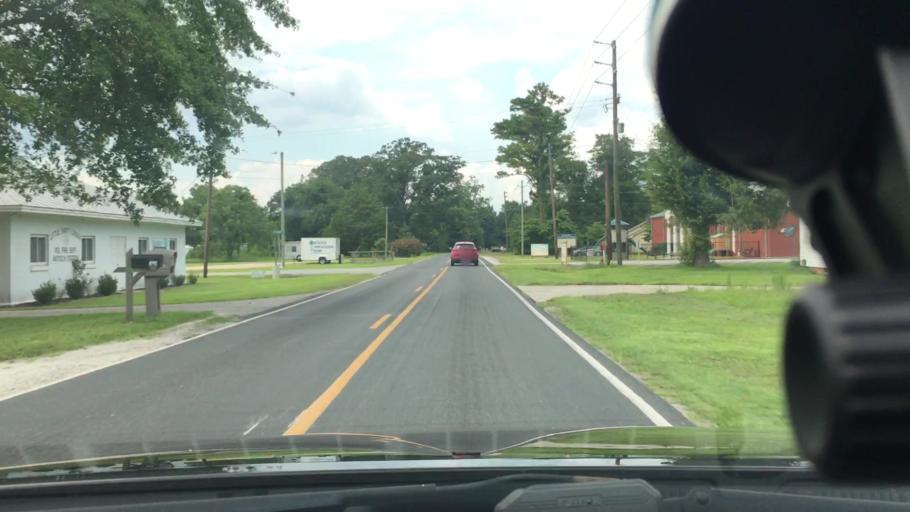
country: US
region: North Carolina
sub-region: Craven County
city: New Bern
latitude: 35.1677
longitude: -77.0498
